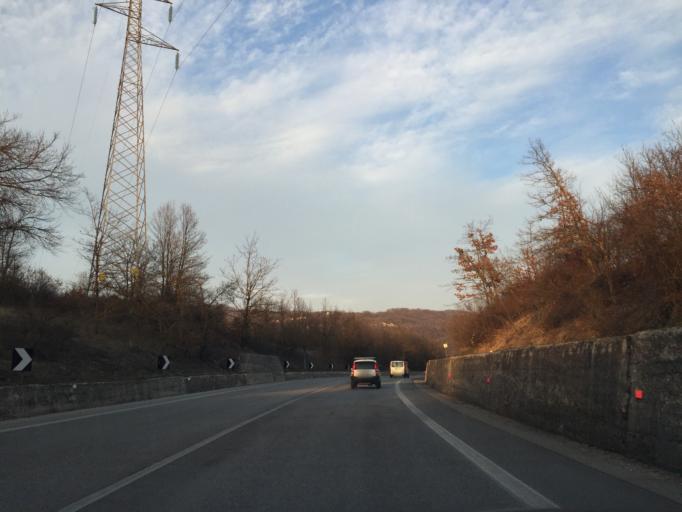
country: IT
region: Molise
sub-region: Provincia di Campobasso
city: Vinchiaturo
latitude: 41.4928
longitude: 14.6043
